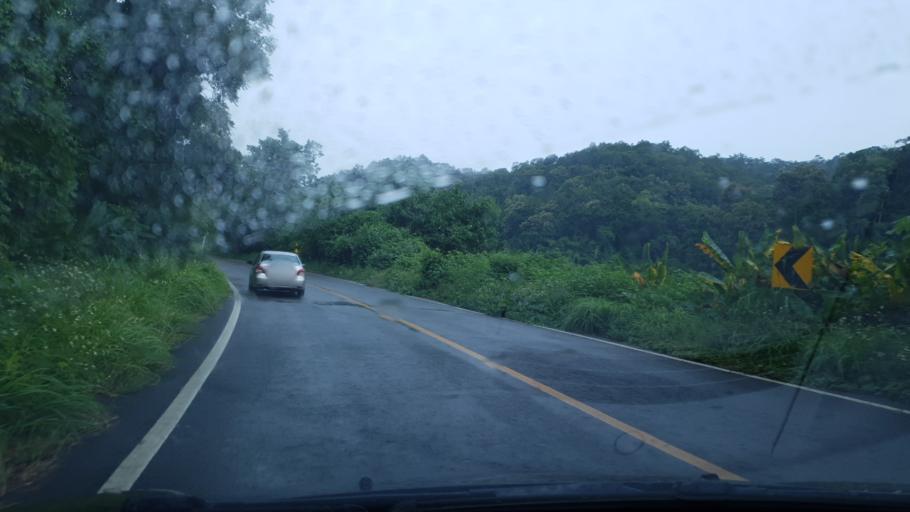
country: TH
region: Mae Hong Son
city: Khun Yuam
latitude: 18.6840
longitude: 97.9197
